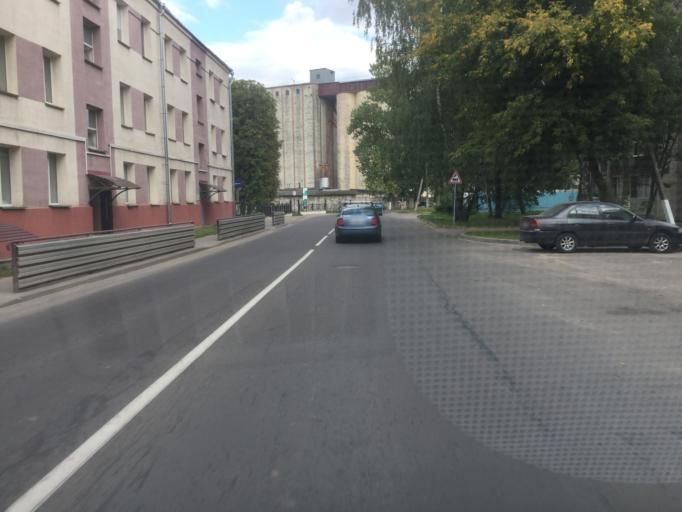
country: BY
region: Vitebsk
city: Vitebsk
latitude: 55.2031
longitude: 30.1863
